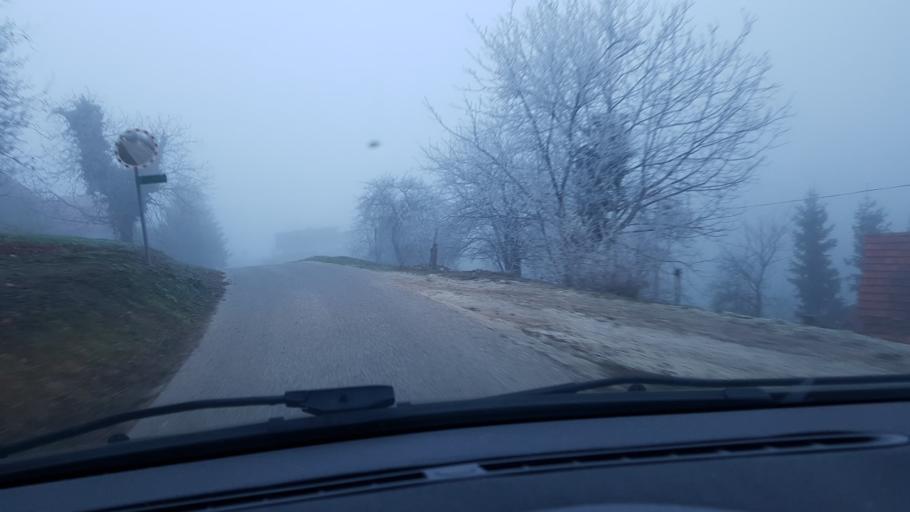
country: HR
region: Krapinsko-Zagorska
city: Pregrada
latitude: 46.1951
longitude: 15.7509
